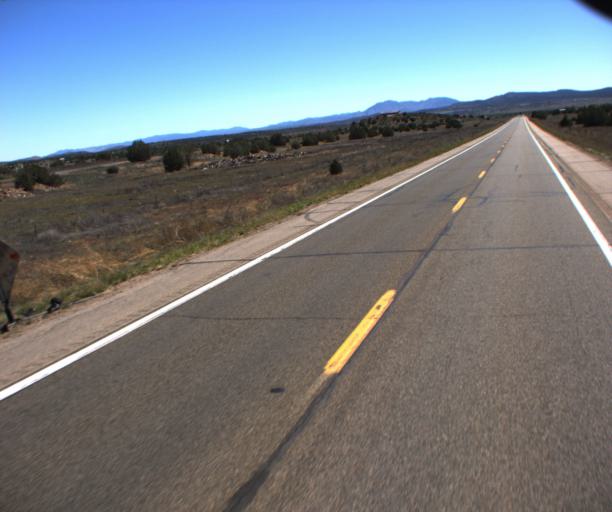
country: US
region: Arizona
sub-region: Yavapai County
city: Paulden
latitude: 34.9208
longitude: -112.4537
